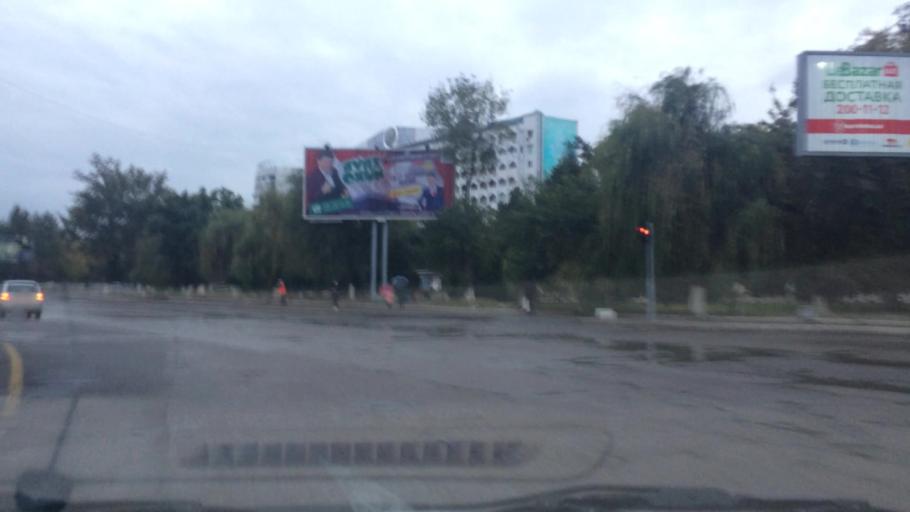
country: UZ
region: Toshkent Shahri
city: Tashkent
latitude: 41.3117
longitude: 69.2404
